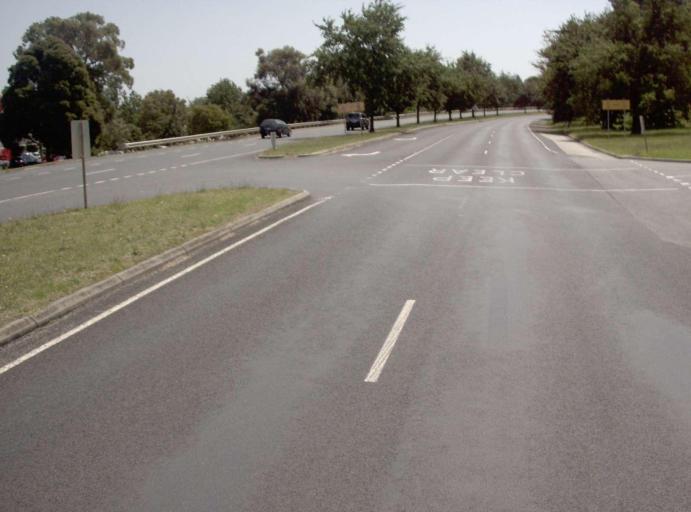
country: AU
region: Victoria
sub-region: Casey
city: Berwick
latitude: -38.0308
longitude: 145.3402
